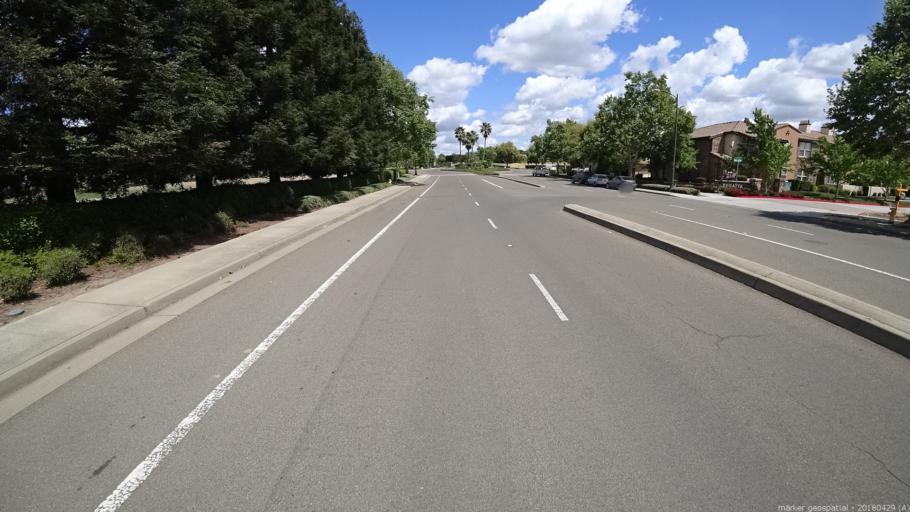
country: US
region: California
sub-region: Yolo County
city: West Sacramento
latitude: 38.5984
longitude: -121.5152
